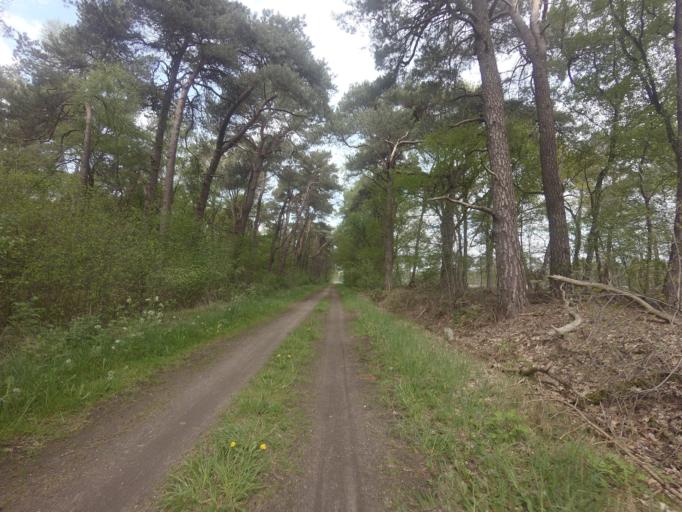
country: NL
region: Overijssel
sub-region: Gemeente Hof van Twente
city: Delden
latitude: 52.2293
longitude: 6.7267
